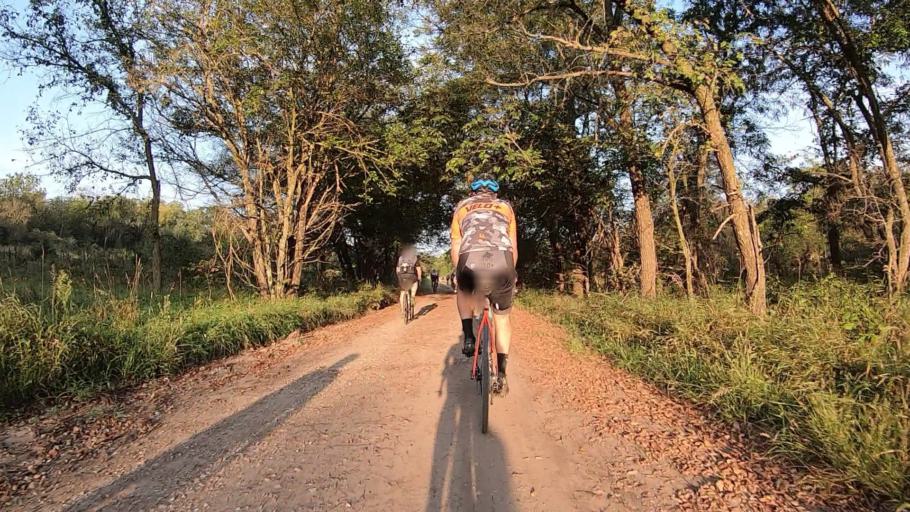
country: US
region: Kansas
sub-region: Marshall County
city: Marysville
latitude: 39.7659
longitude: -96.6991
